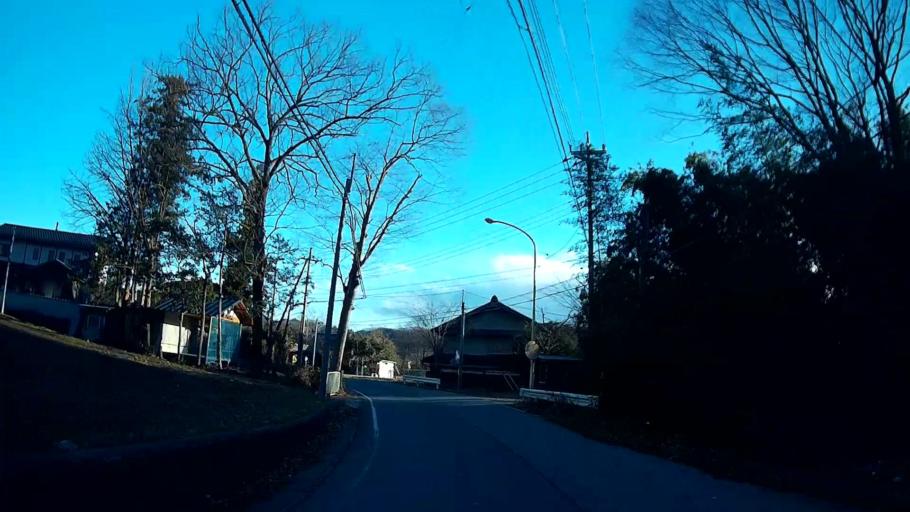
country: JP
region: Saitama
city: Chichibu
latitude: 36.0441
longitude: 139.0140
